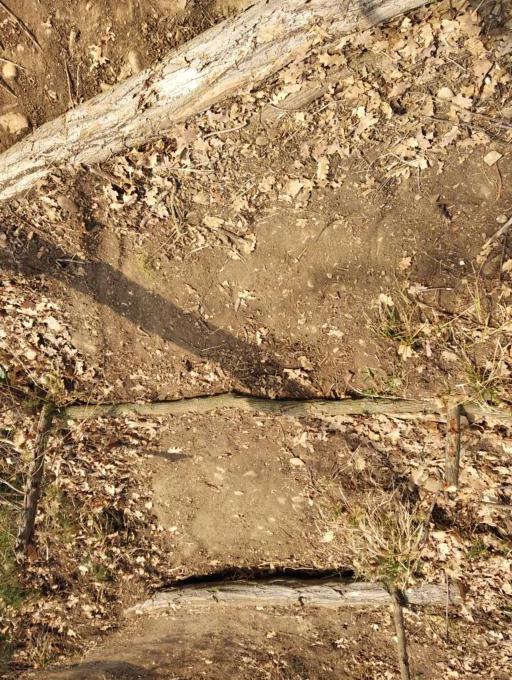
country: IT
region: Emilia-Romagna
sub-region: Provincia di Bologna
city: Ponticella
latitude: 44.4521
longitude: 11.3761
